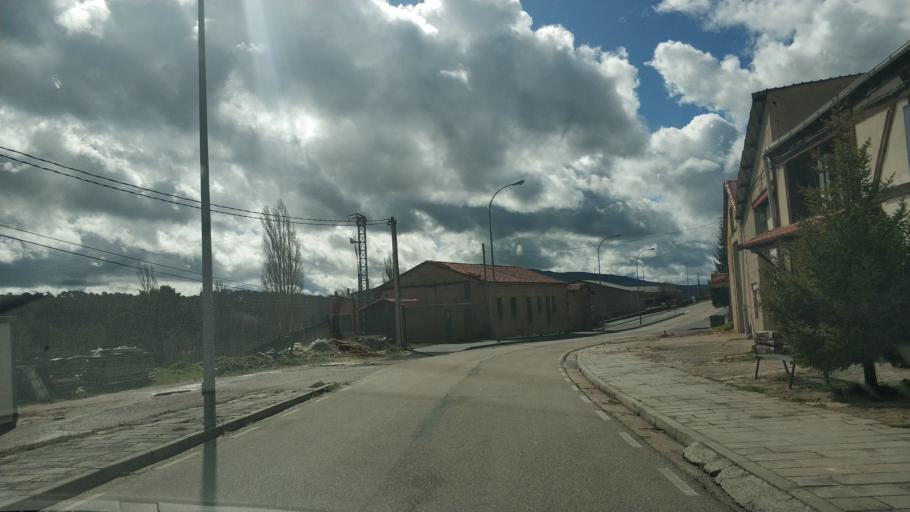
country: ES
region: Castille and Leon
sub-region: Provincia de Burgos
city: Quintanar de la Sierra
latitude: 41.9865
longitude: -3.0293
